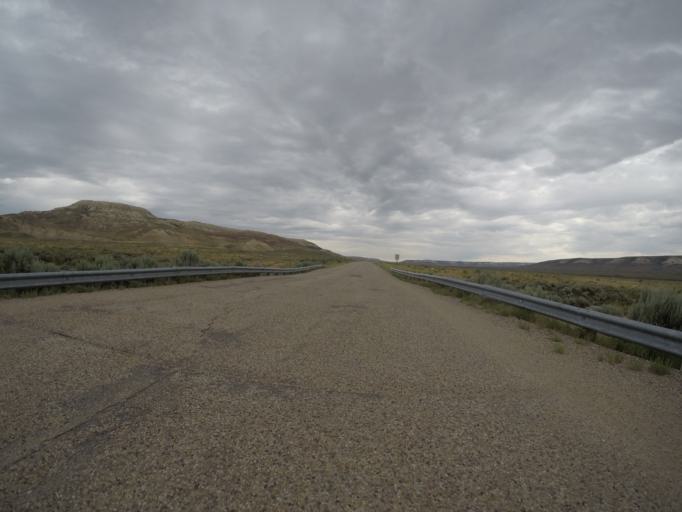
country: US
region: Wyoming
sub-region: Lincoln County
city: Kemmerer
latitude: 41.8230
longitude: -110.7605
